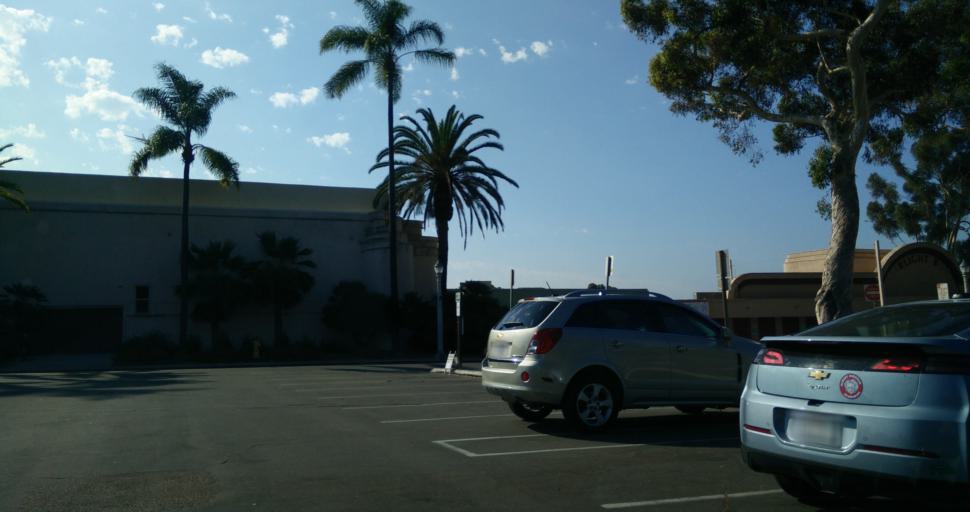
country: US
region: California
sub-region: San Diego County
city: San Diego
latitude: 32.7271
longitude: -117.1537
